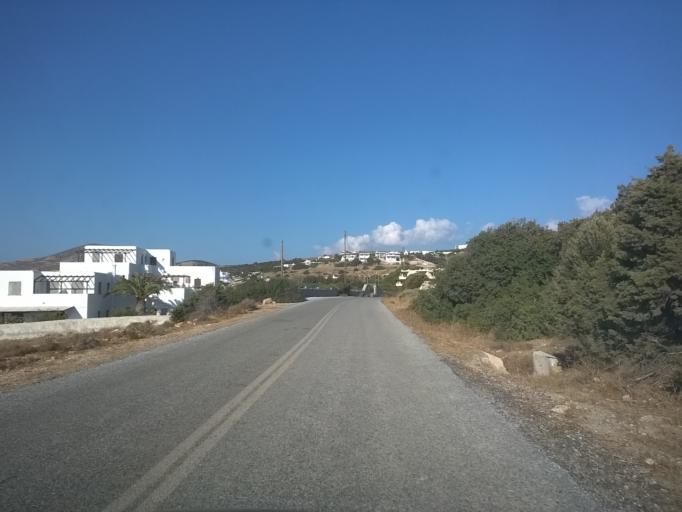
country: GR
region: South Aegean
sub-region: Nomos Kykladon
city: Naxos
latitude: 36.9885
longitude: 25.3942
